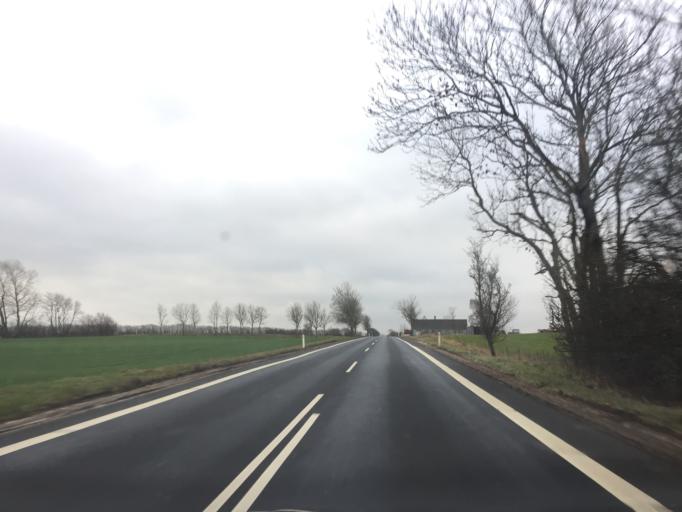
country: DK
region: South Denmark
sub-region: Svendborg Kommune
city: Thuro By
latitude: 55.1338
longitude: 10.6708
